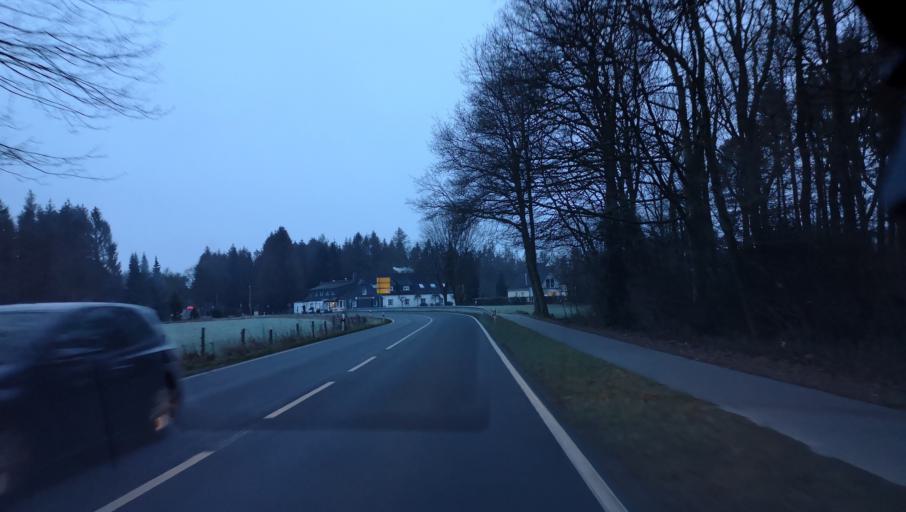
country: DE
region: North Rhine-Westphalia
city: Radevormwald
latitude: 51.2126
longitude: 7.3886
